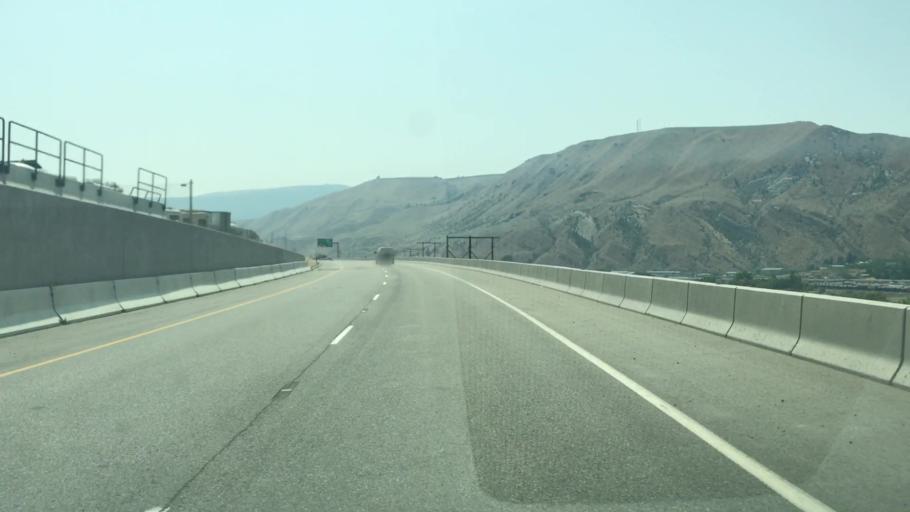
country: US
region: Washington
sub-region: Douglas County
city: East Wenatchee
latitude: 47.4044
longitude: -120.2916
